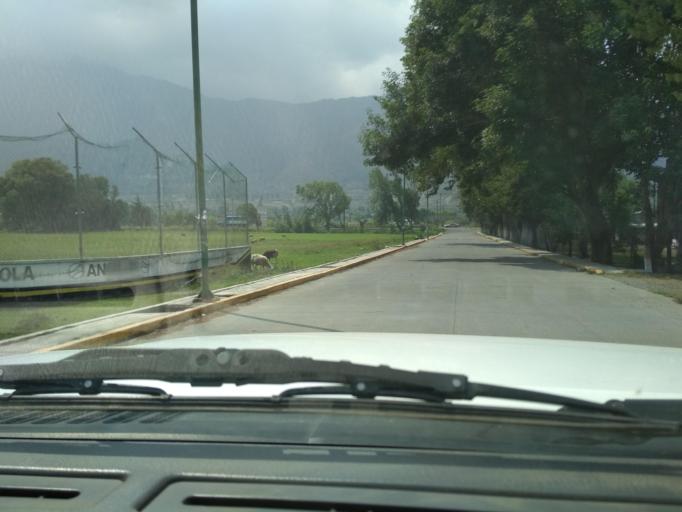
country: MX
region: Veracruz
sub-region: Acultzingo
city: Acatla
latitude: 18.7665
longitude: -97.2194
